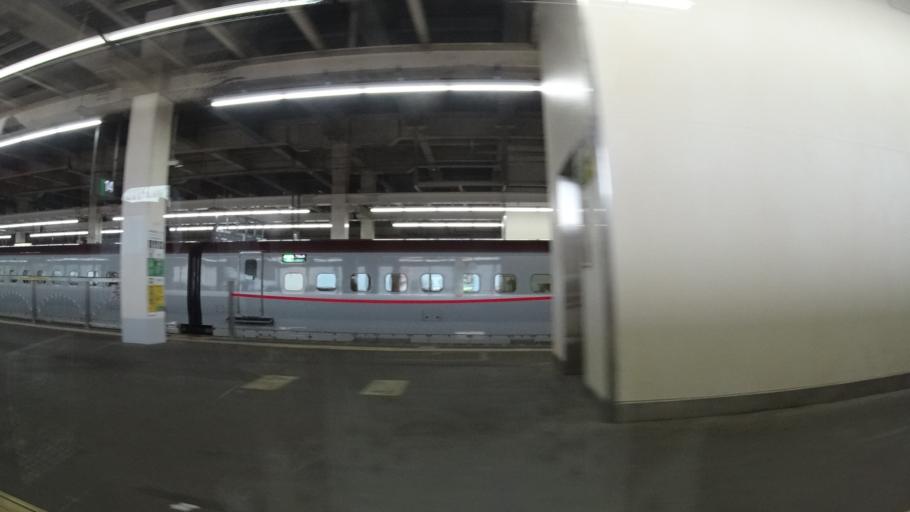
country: JP
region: Saitama
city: Yono
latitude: 35.9072
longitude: 139.6231
